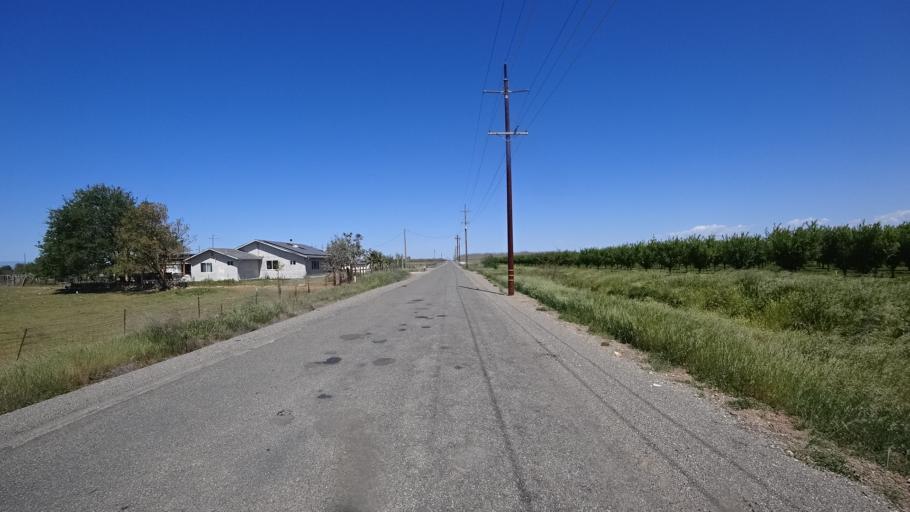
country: US
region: California
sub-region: Glenn County
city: Orland
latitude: 39.7737
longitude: -122.1409
